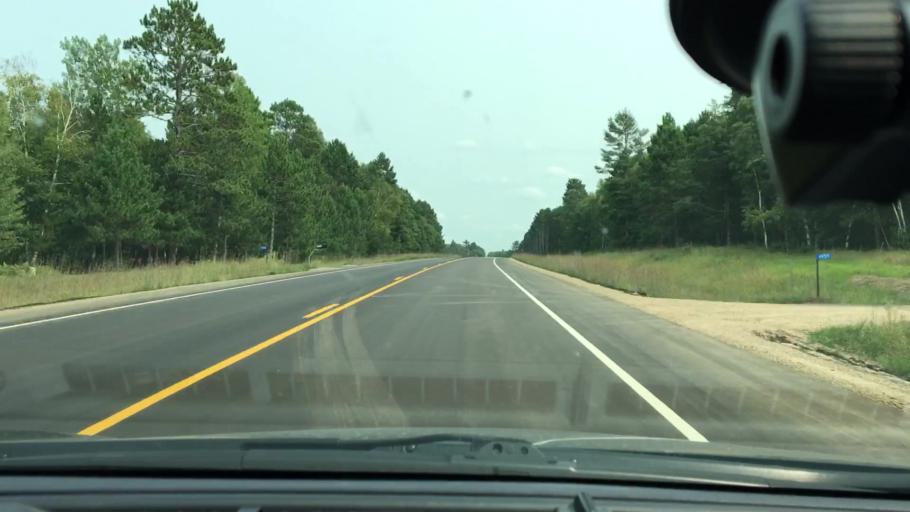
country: US
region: Minnesota
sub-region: Crow Wing County
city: Nisswa
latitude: 46.5292
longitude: -94.2571
